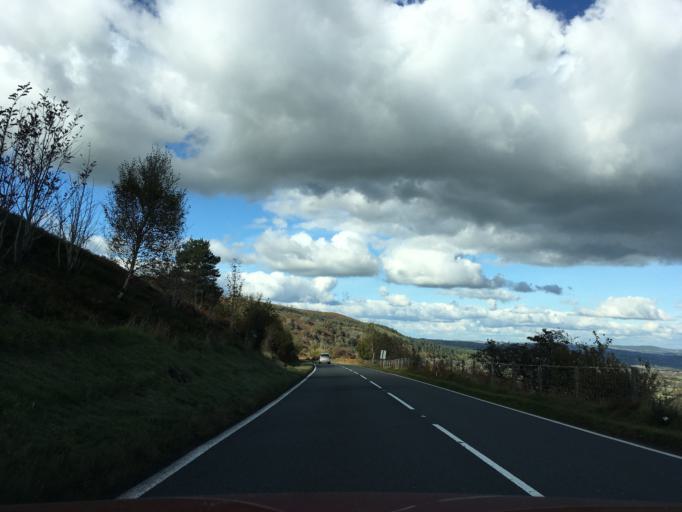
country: GB
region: Wales
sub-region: Sir Powys
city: Brecon
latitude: 51.8851
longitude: -3.4941
